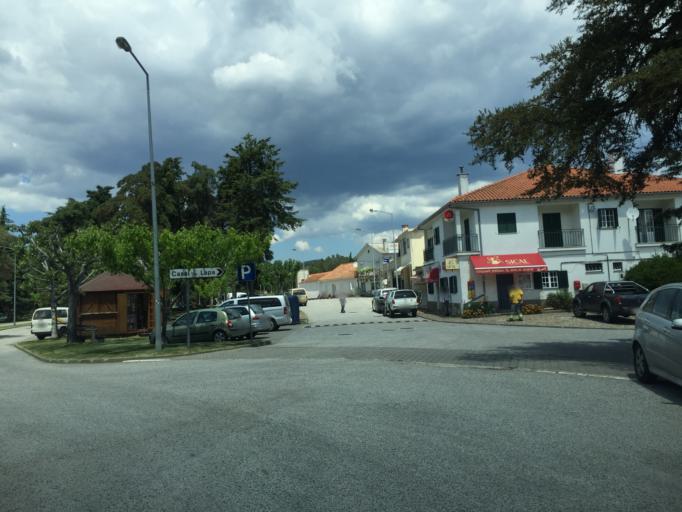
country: PT
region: Coimbra
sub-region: Pampilhosa da Serra
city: Pampilhosa da Serra
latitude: 40.0894
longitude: -7.8500
